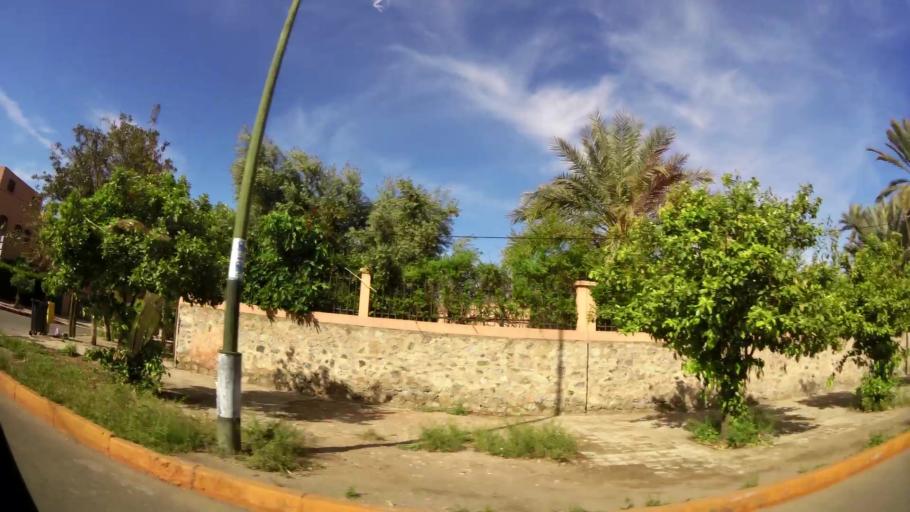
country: MA
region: Marrakech-Tensift-Al Haouz
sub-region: Marrakech
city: Marrakesh
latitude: 31.6511
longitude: -8.0056
